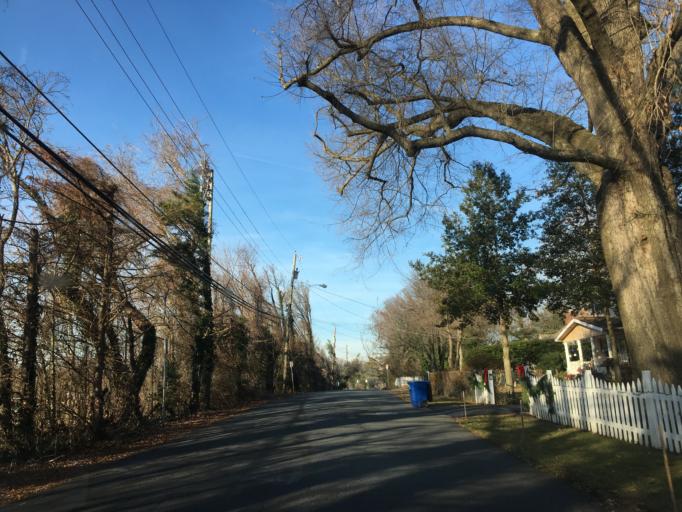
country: US
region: Virginia
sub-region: City of Fairfax
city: Fairfax
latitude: 38.8547
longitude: -77.3120
